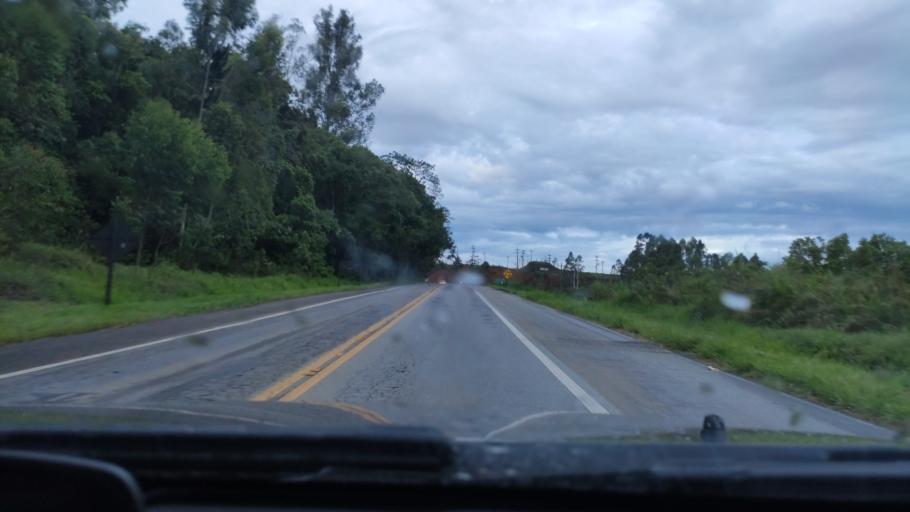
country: BR
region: Sao Paulo
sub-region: Braganca Paulista
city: Braganca Paulista
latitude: -22.8183
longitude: -46.5477
